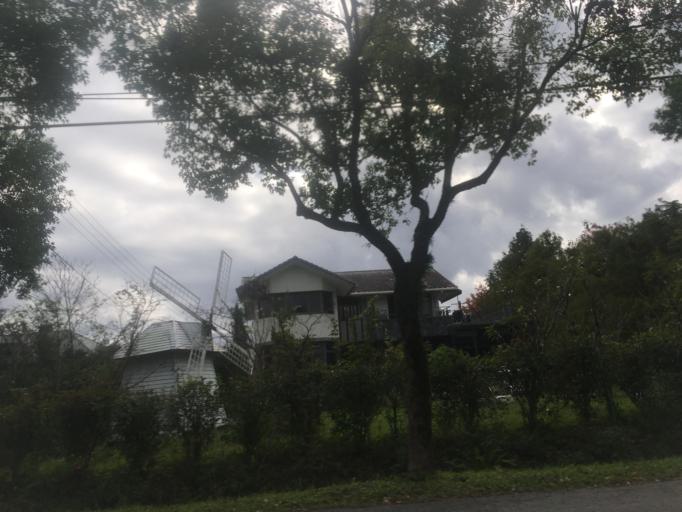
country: TW
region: Taiwan
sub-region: Yilan
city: Yilan
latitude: 24.6721
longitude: 121.6677
